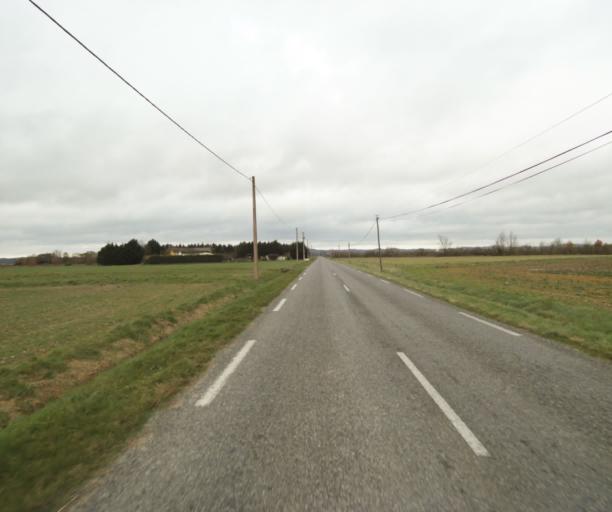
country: FR
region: Midi-Pyrenees
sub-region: Departement de l'Ariege
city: Mazeres
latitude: 43.2271
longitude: 1.6466
